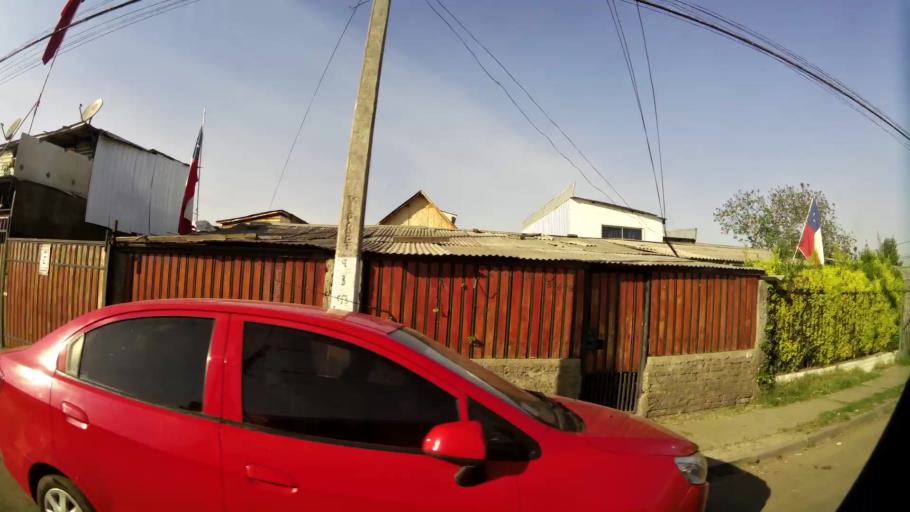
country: CL
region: Santiago Metropolitan
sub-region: Provincia de Santiago
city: Lo Prado
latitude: -33.4378
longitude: -70.7453
